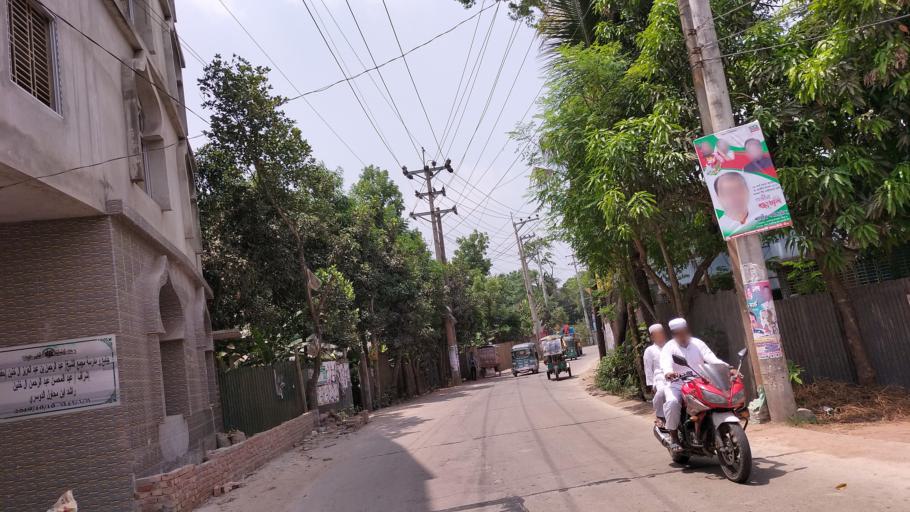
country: BD
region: Dhaka
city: Azimpur
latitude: 23.7333
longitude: 90.2634
